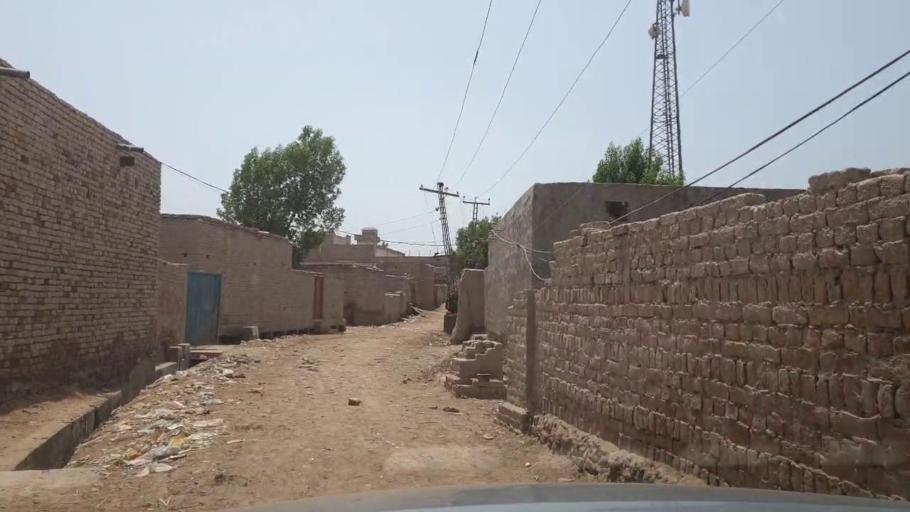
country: PK
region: Sindh
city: Madeji
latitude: 27.7617
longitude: 68.3831
